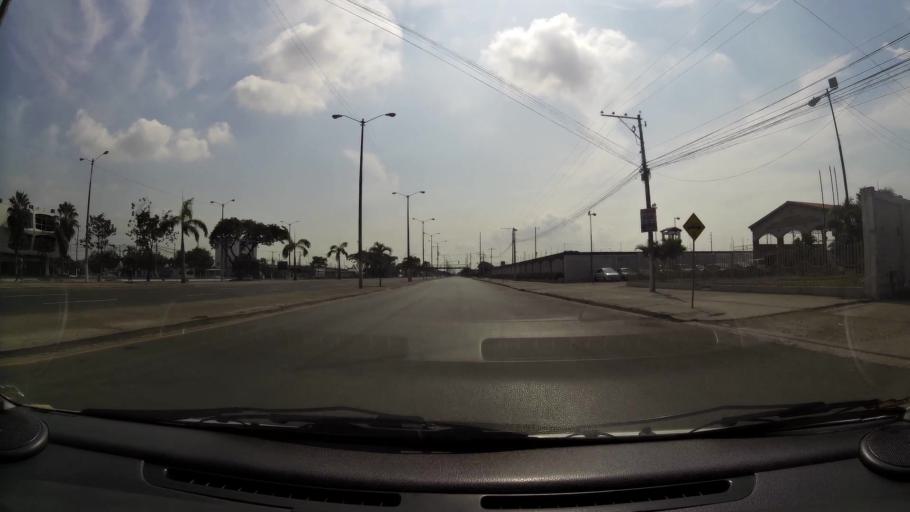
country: EC
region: Guayas
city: Guayaquil
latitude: -2.2724
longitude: -79.9035
